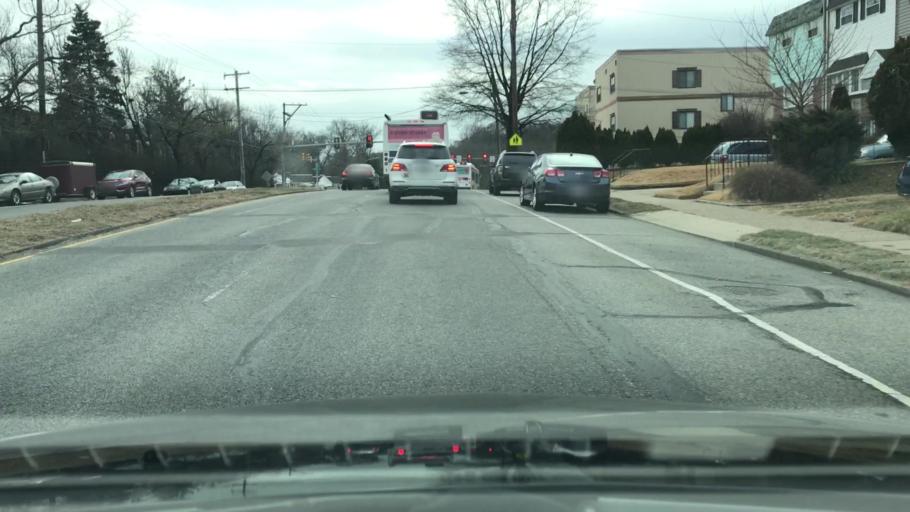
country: US
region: Pennsylvania
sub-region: Bucks County
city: Cornwells Heights
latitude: 40.0908
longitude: -74.9835
